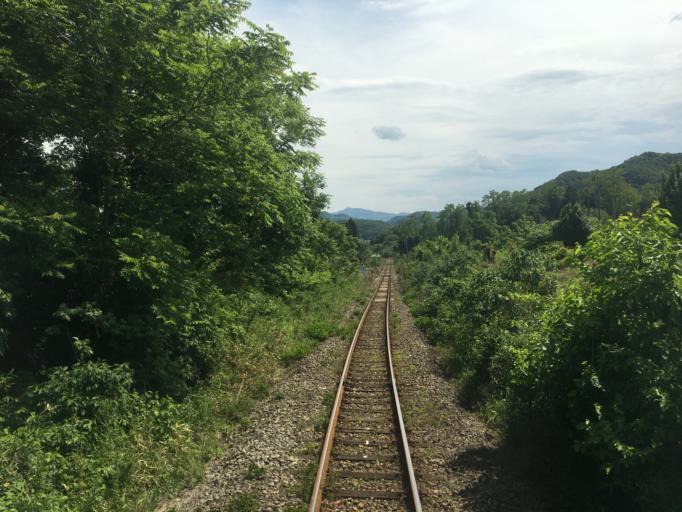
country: JP
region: Saitama
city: Yorii
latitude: 36.1046
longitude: 139.1931
